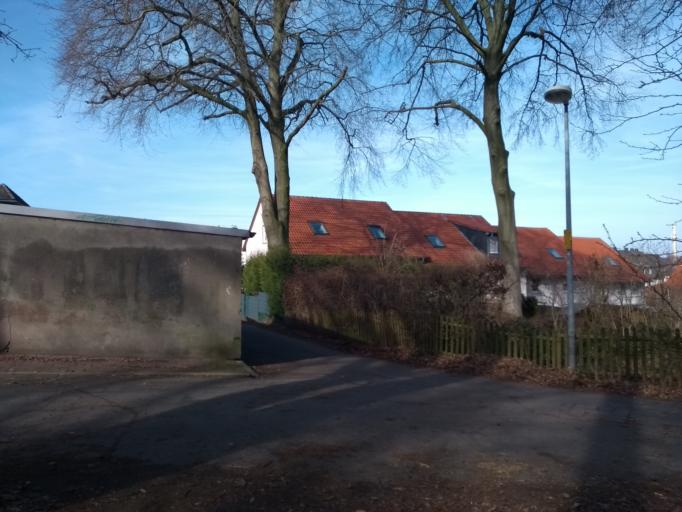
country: DE
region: North Rhine-Westphalia
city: Lunen
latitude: 51.6250
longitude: 7.4879
